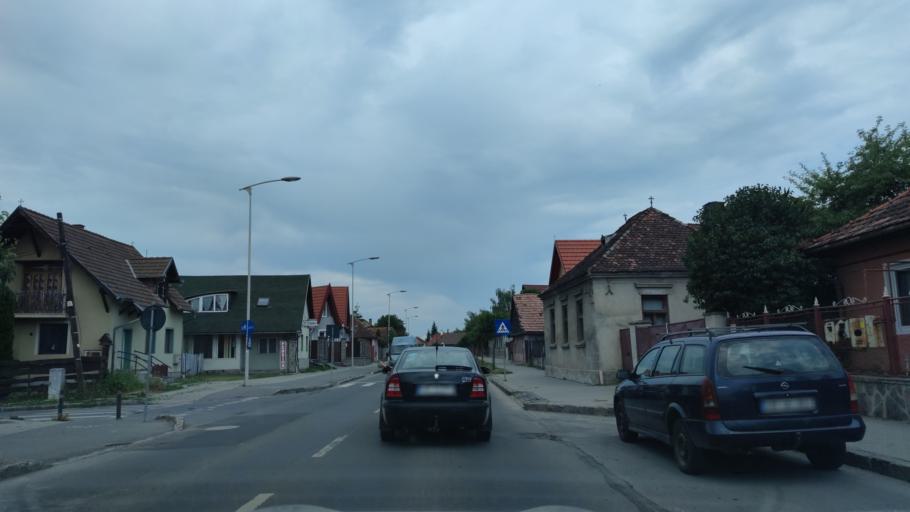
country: RO
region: Harghita
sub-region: Municipiul Miercurea Ciuc
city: Miercurea-Ciuc
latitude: 46.3741
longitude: 25.8025
